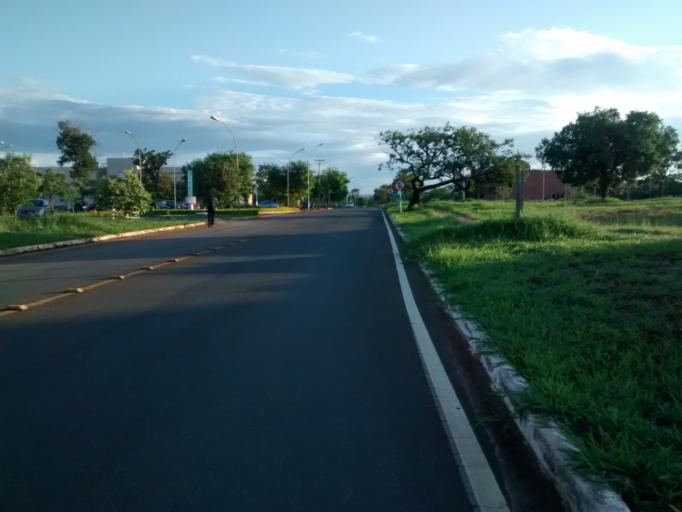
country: BR
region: Federal District
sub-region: Brasilia
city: Brasilia
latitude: -15.7711
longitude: -47.8664
